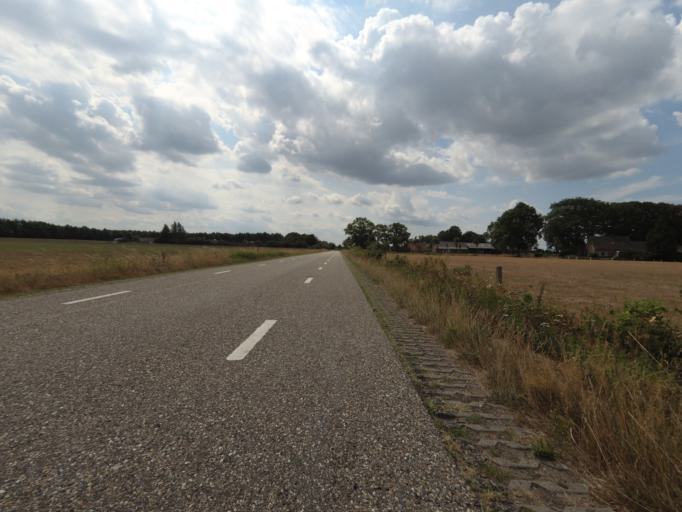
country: NL
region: Overijssel
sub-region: Gemeente Hof van Twente
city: Hengevelde
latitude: 52.1617
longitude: 6.6797
